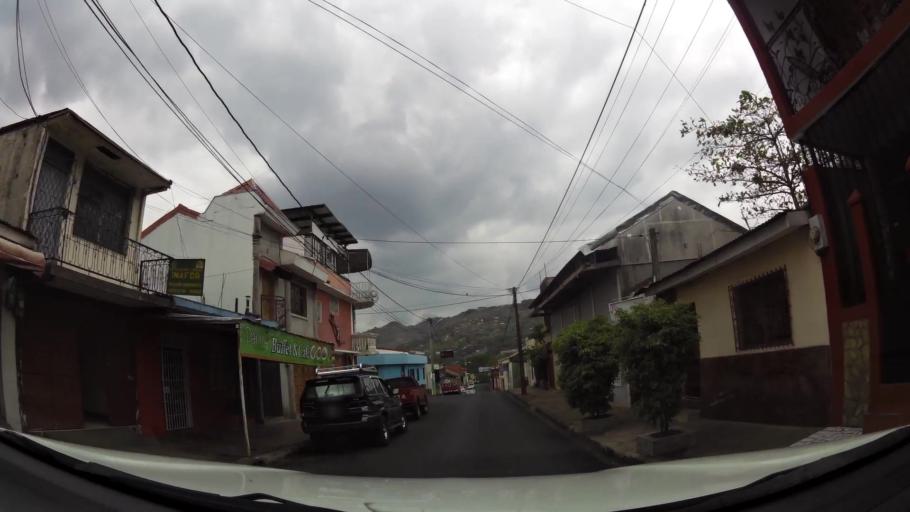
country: NI
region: Matagalpa
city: Matagalpa
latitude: 12.9236
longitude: -85.9183
